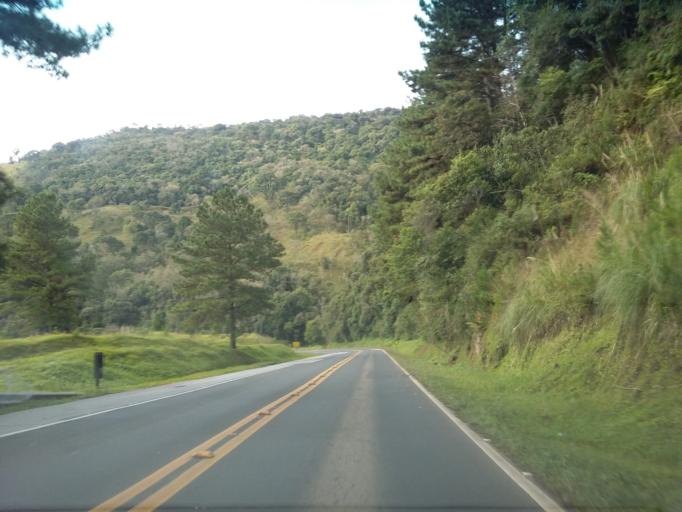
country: BR
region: Santa Catarina
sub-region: Santa Cecilia
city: Santa Cecilia
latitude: -26.7553
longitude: -50.3316
